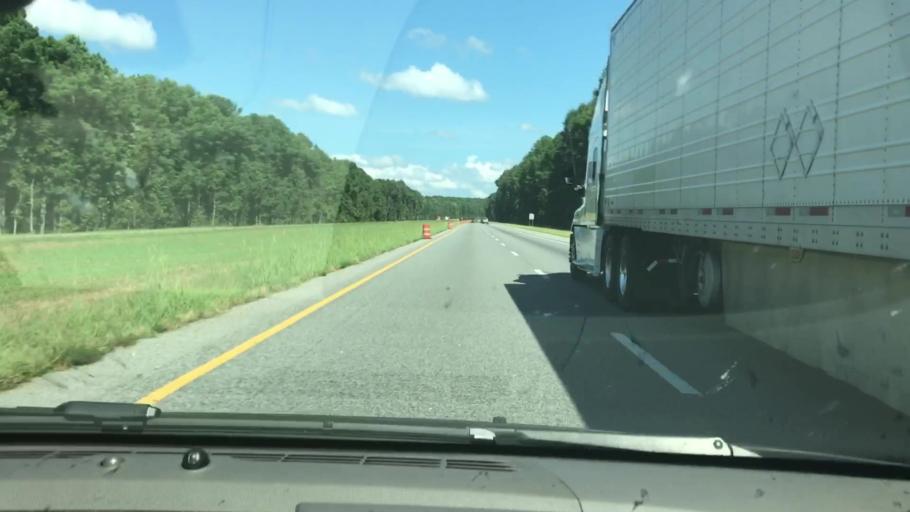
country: US
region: Georgia
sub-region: Harris County
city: Hamilton
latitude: 32.7088
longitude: -85.0121
